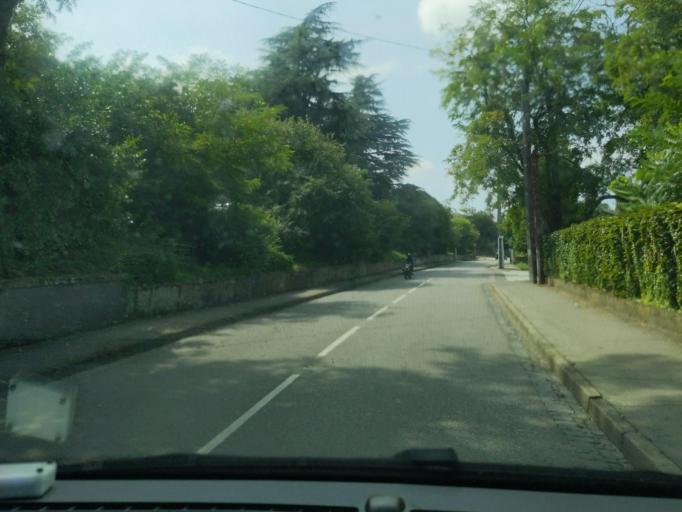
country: FR
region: Midi-Pyrenees
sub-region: Departement de la Haute-Garonne
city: Balma
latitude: 43.6053
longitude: 1.4774
